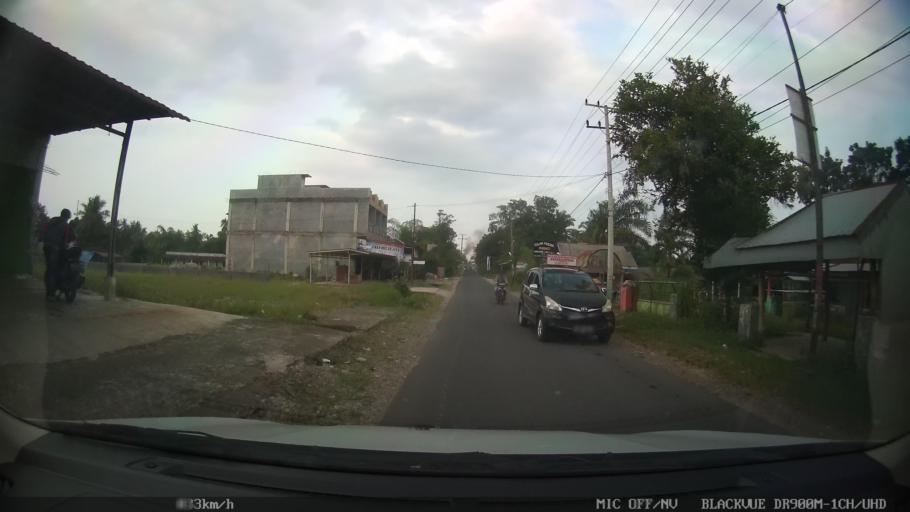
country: ID
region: North Sumatra
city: Sunggal
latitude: 3.5610
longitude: 98.5721
